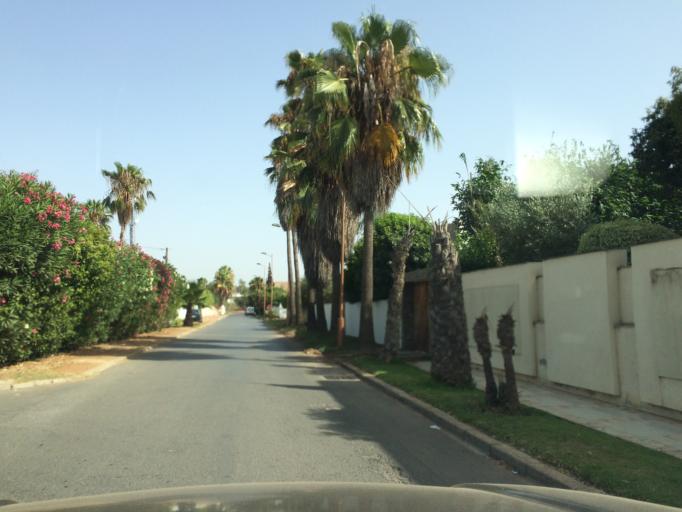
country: MA
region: Rabat-Sale-Zemmour-Zaer
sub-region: Rabat
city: Rabat
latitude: 33.9891
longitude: -6.8334
